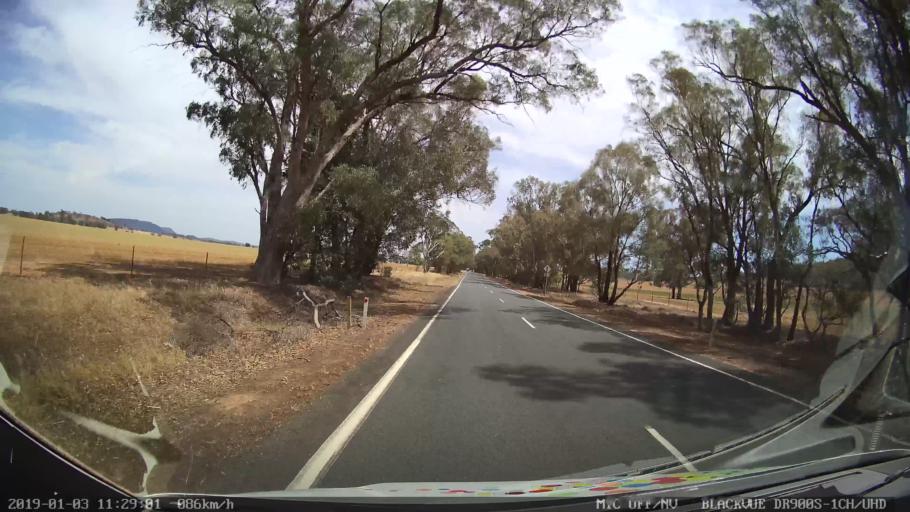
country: AU
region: New South Wales
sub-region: Weddin
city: Grenfell
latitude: -33.9965
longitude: 148.2027
